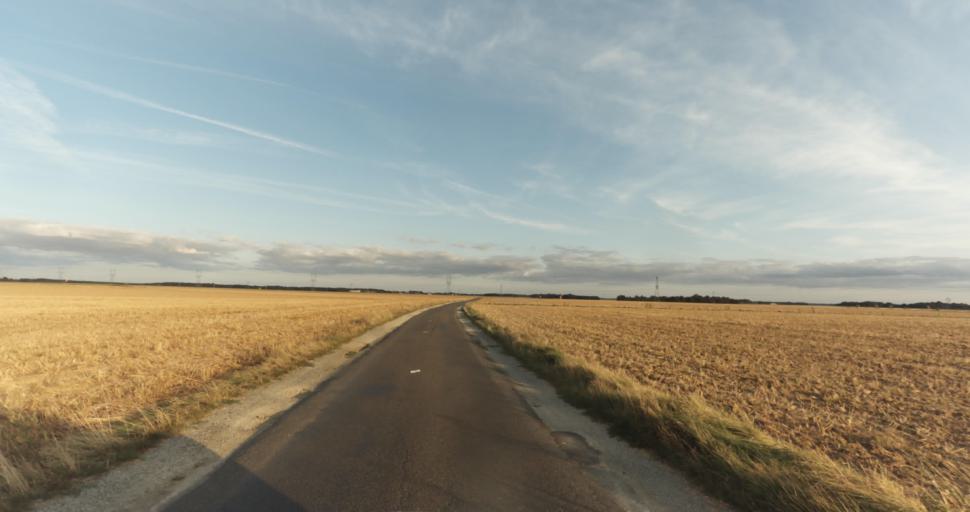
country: FR
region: Haute-Normandie
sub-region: Departement de l'Eure
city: Saint-Germain-sur-Avre
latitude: 48.8626
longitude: 1.2517
